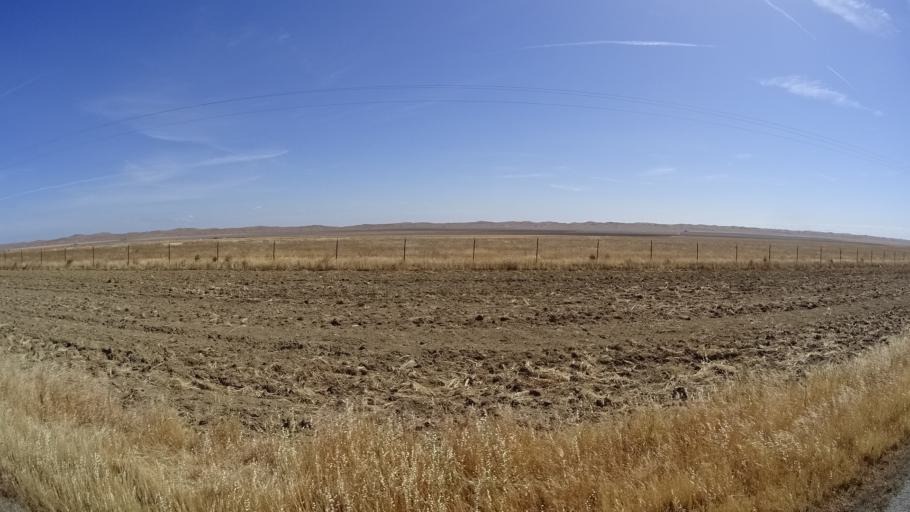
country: US
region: California
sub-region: Kings County
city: Avenal
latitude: 35.9195
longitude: -120.0718
